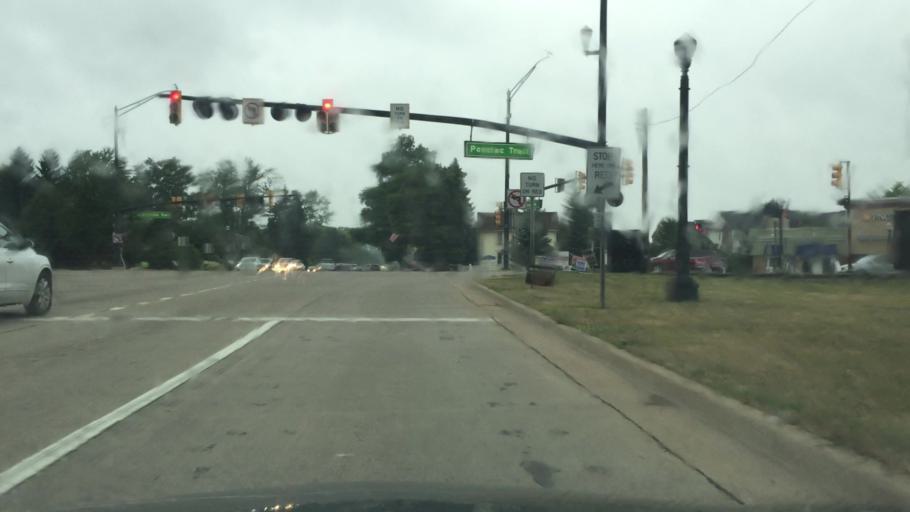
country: US
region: Michigan
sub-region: Oakland County
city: Wixom
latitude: 42.5239
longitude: -83.5358
